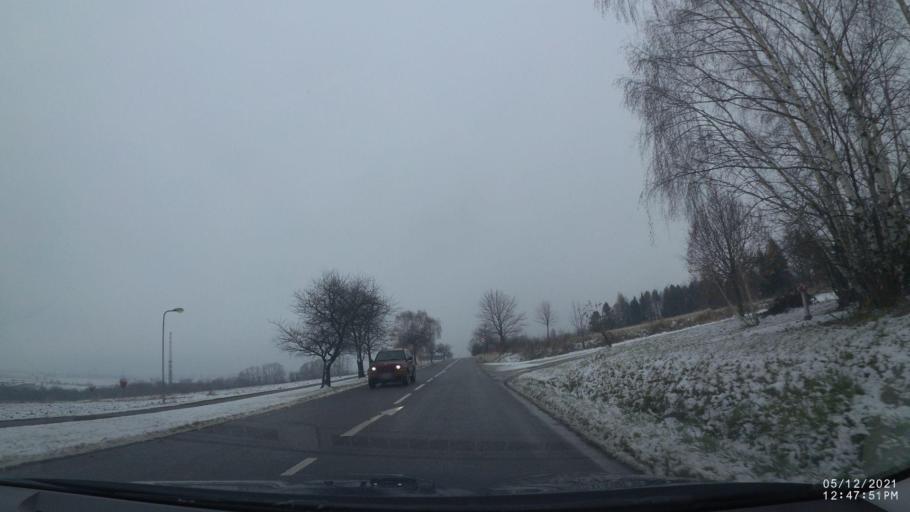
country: CZ
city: Nove Mesto nad Metuji
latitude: 50.3619
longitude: 16.1470
